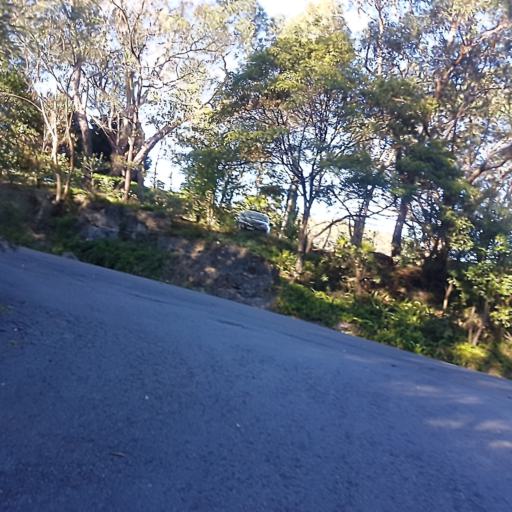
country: AU
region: New South Wales
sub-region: Ku-ring-gai
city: Roseville Chase
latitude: -33.7764
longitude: 151.2045
